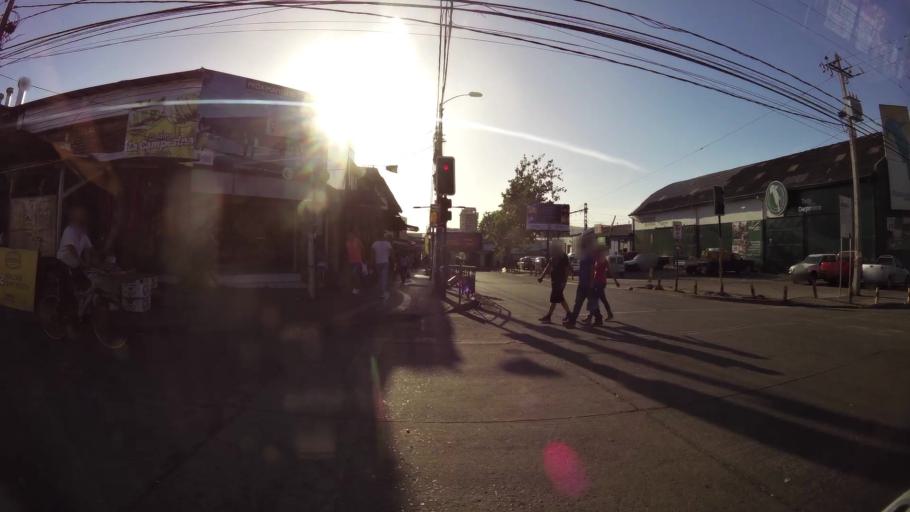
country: CL
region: Maule
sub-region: Provincia de Talca
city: Talca
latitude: -35.4287
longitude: -71.6480
